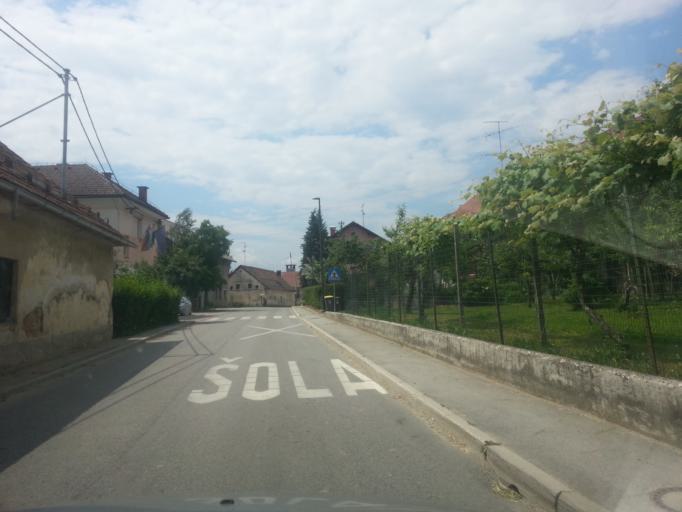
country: SI
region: Log-Dragomer
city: Log pri Brezovici
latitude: 46.0279
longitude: 14.3475
